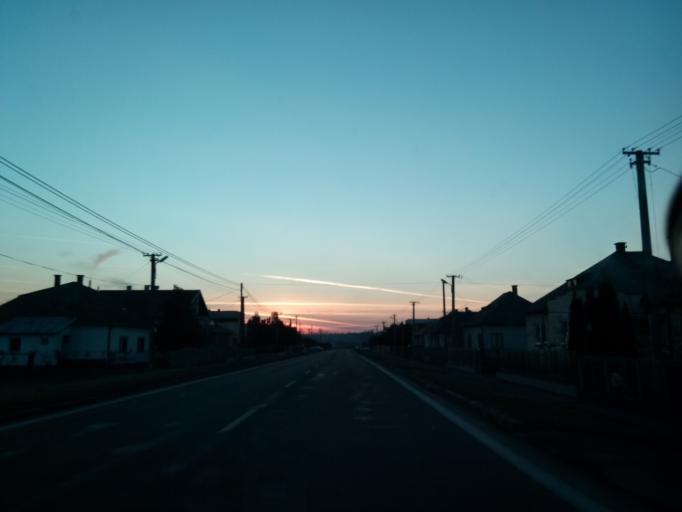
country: SK
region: Kosicky
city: Vinne
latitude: 48.7660
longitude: 22.0615
